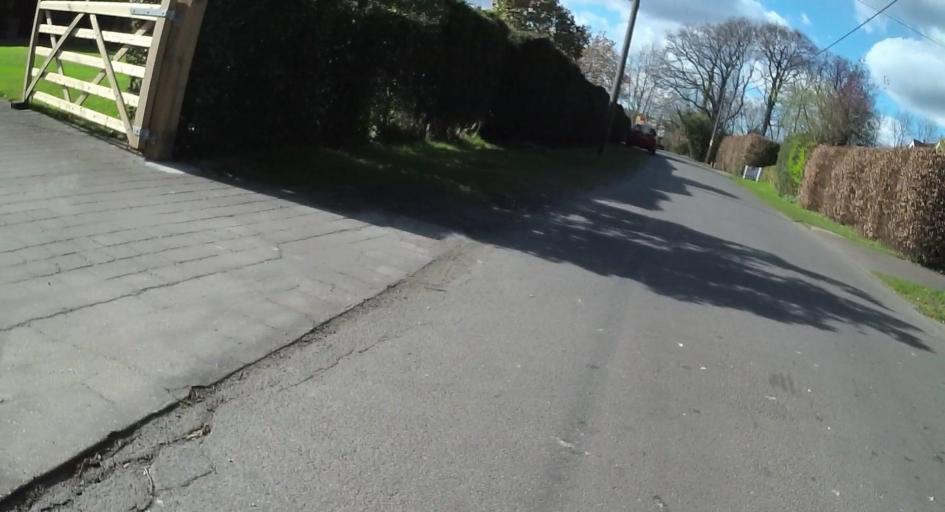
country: GB
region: England
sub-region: Surrey
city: Windlesham
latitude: 51.3378
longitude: -0.6504
